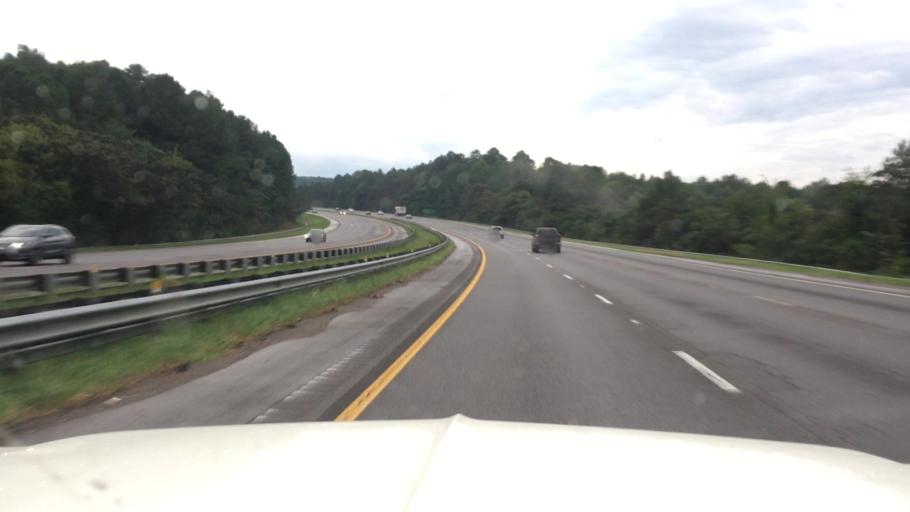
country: US
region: Alabama
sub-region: Jefferson County
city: Mount Olive
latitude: 33.7059
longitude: -86.8366
